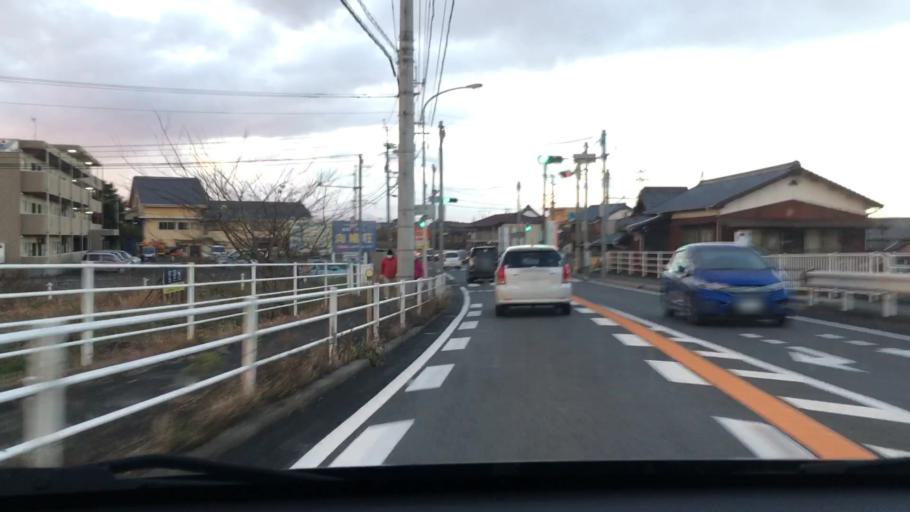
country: JP
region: Fukuoka
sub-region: Buzen-shi
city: Buzen
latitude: 33.6217
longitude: 131.0947
